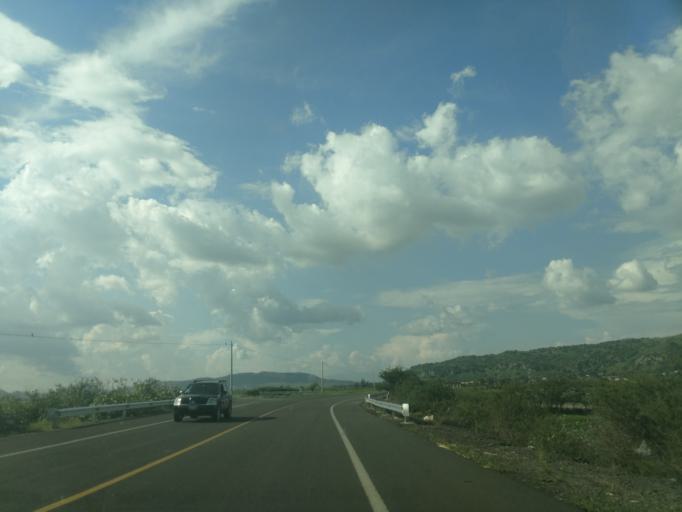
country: MX
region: Jalisco
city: Antonio Escobedo
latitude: 20.9000
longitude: -103.9949
